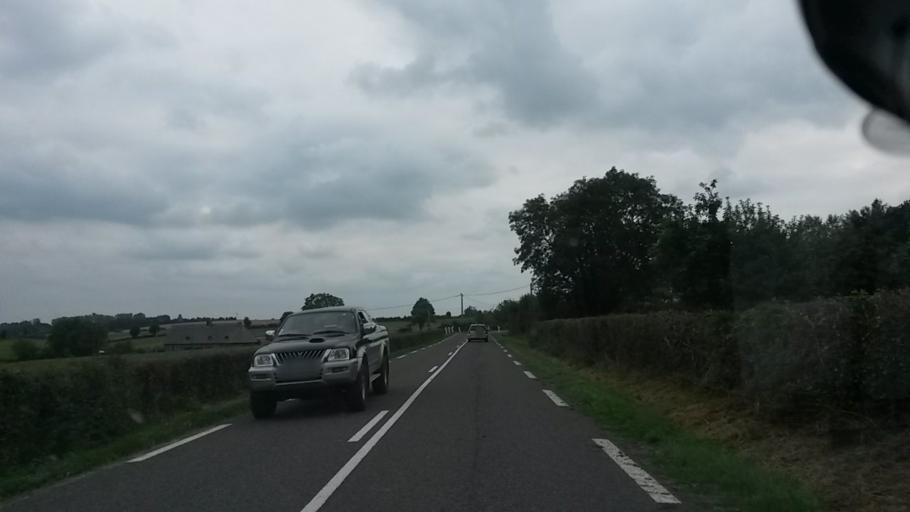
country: FR
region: Haute-Normandie
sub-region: Departement de la Seine-Maritime
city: Forges-les-Eaux
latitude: 49.5661
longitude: 1.5298
